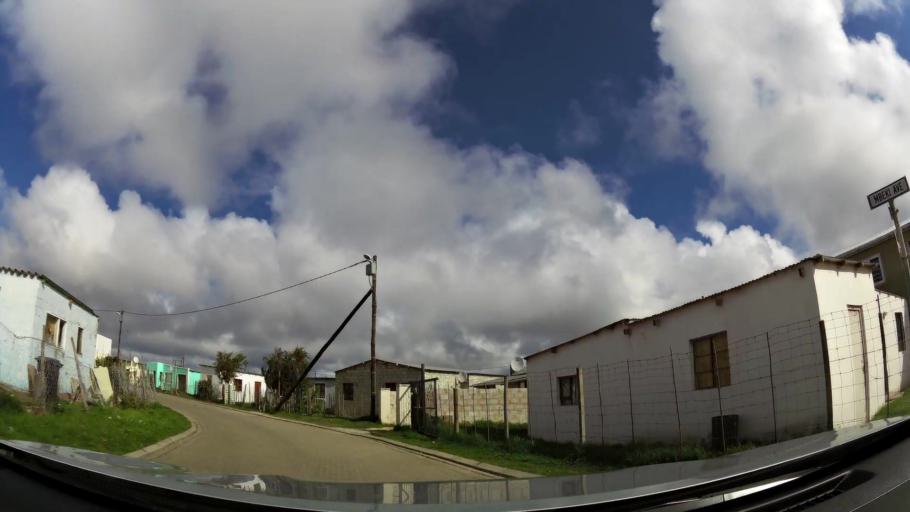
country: ZA
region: Western Cape
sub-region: Eden District Municipality
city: Plettenberg Bay
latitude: -34.0562
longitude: 23.3167
